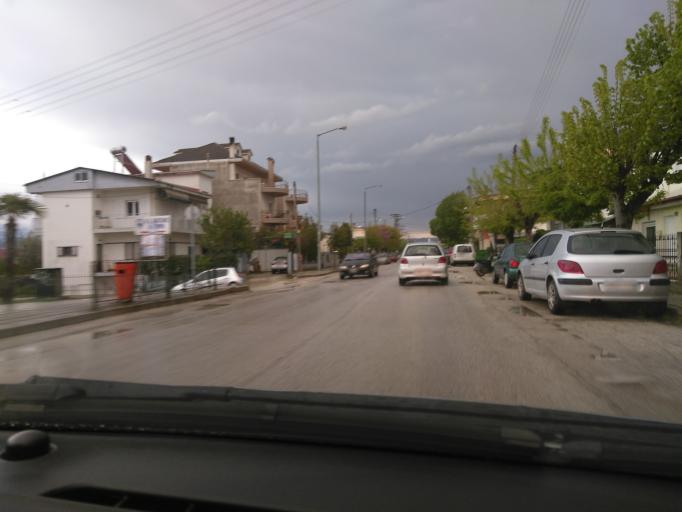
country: GR
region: Epirus
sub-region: Nomos Ioanninon
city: Anatoli
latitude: 39.6396
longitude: 20.8684
